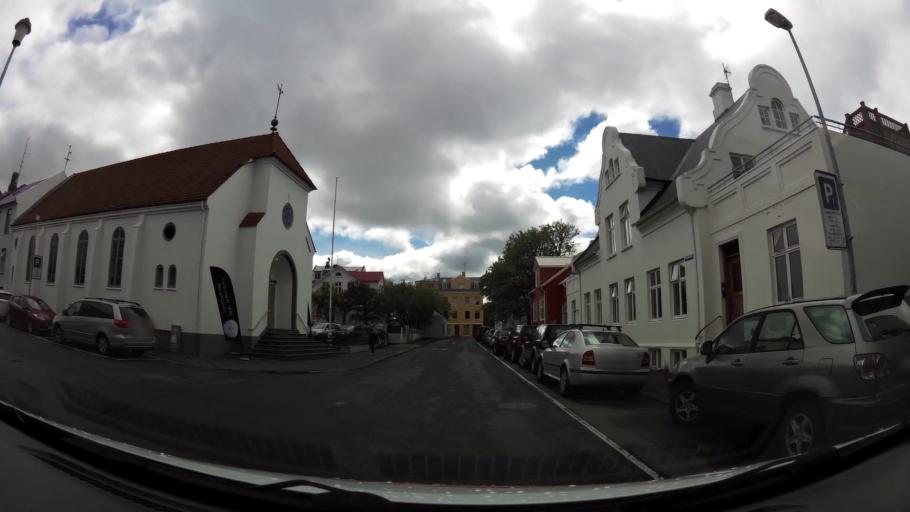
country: IS
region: Capital Region
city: Kopavogur
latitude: 64.1456
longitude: -21.9346
